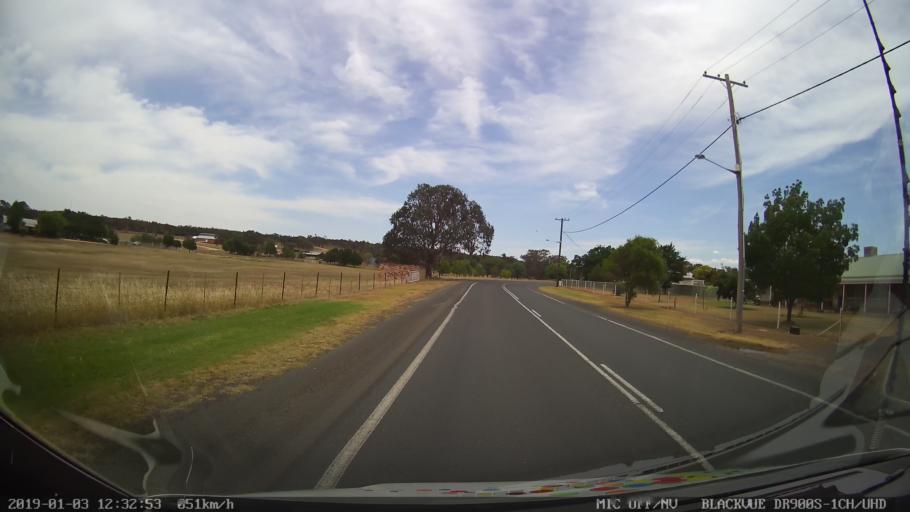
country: AU
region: New South Wales
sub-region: Weddin
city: Grenfell
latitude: -33.8895
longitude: 148.1621
